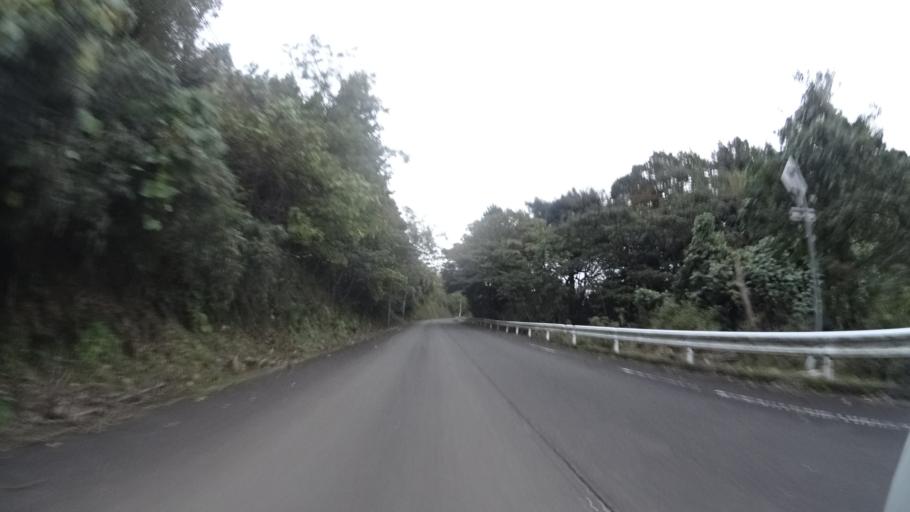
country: JP
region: Kyoto
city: Maizuru
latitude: 35.5652
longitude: 135.4625
